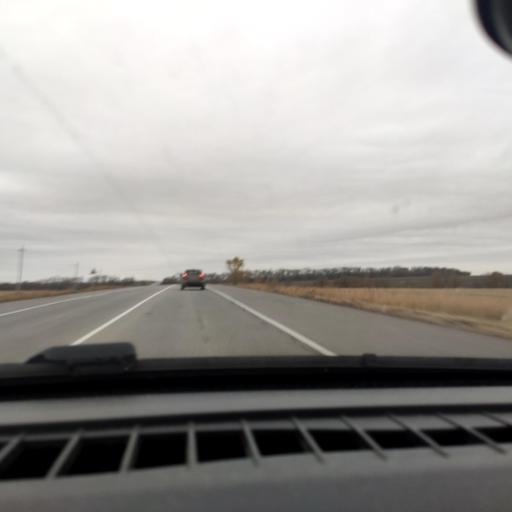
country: RU
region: Voronezj
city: Devitsa
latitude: 51.5775
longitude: 38.9750
